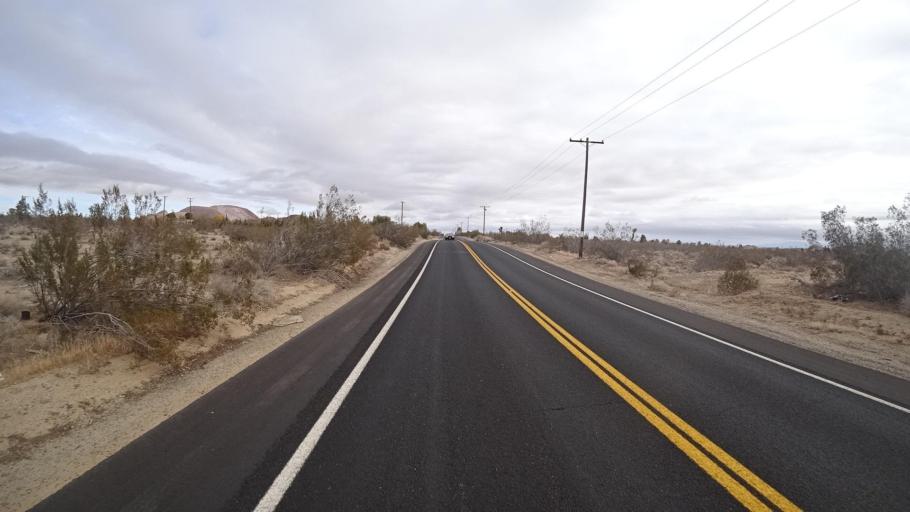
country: US
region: California
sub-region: Kern County
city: Rosamond
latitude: 34.9509
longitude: -118.2423
